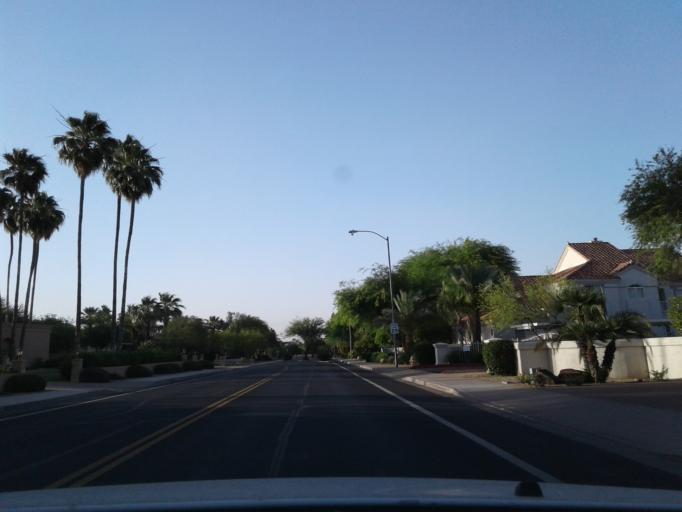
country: US
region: Arizona
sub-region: Maricopa County
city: Paradise Valley
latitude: 33.5802
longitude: -111.9692
